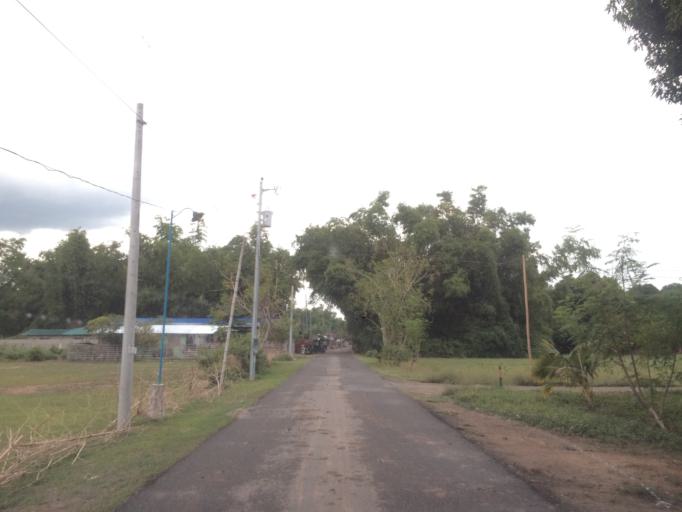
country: PH
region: Ilocos
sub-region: Province of Pangasinan
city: Anambongan
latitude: 15.8709
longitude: 120.3877
